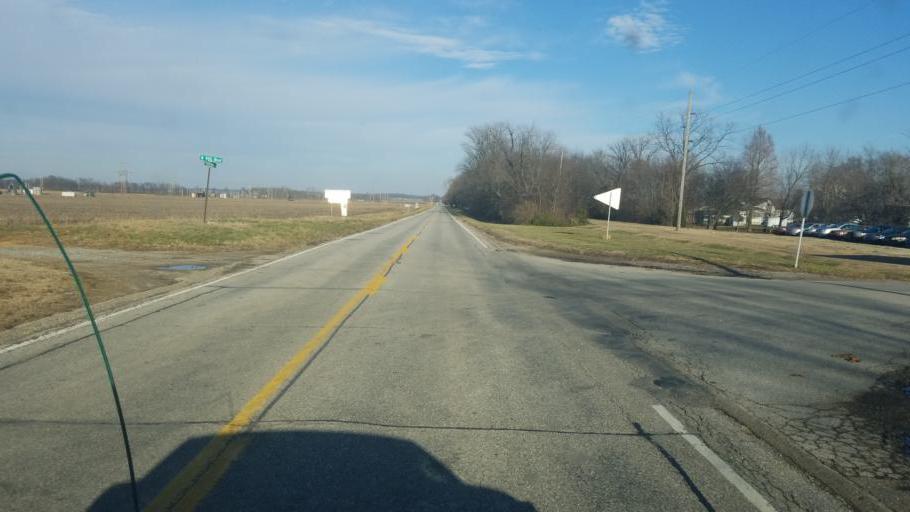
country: US
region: Illinois
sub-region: Wabash County
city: Mount Carmel
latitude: 38.3527
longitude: -87.8674
